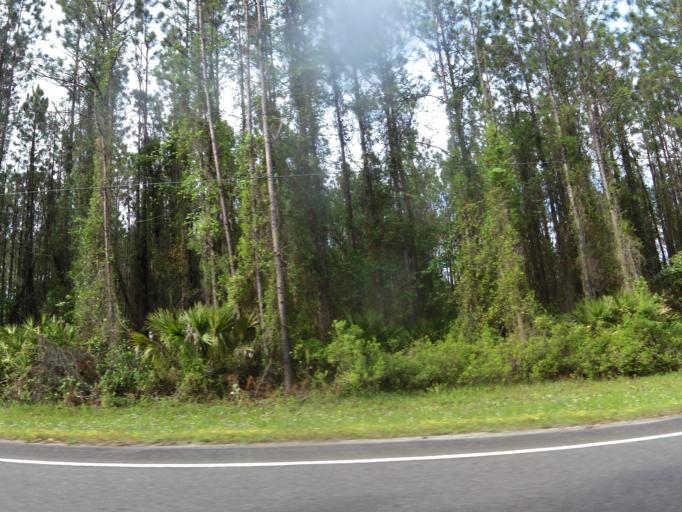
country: US
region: Florida
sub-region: Nassau County
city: Yulee
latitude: 30.6917
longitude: -81.6789
